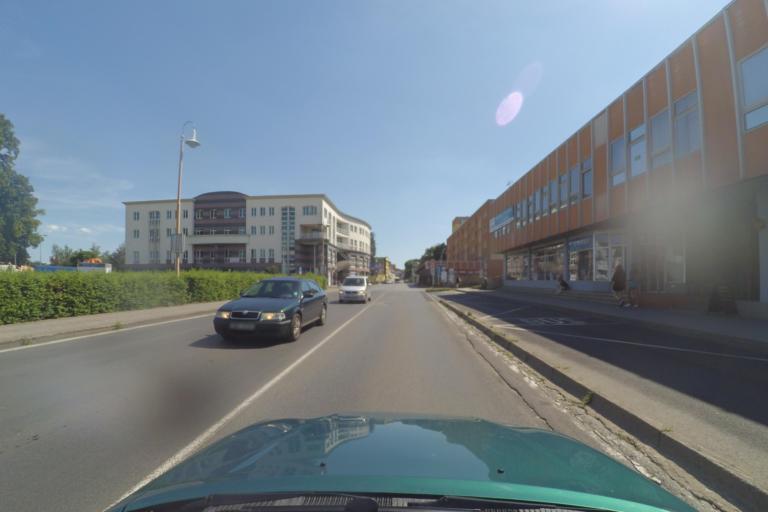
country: CZ
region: Liberecky
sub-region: Okres Ceska Lipa
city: Ceska Lipa
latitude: 50.6820
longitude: 14.5366
